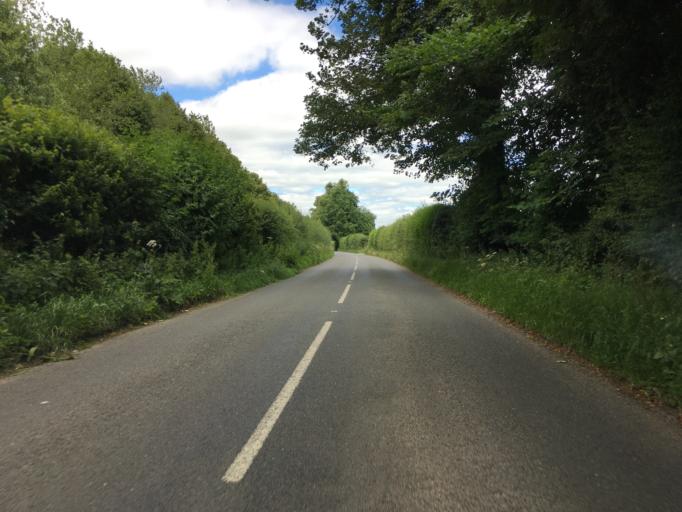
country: GB
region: England
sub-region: West Berkshire
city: Welford
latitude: 51.4583
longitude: -1.4124
